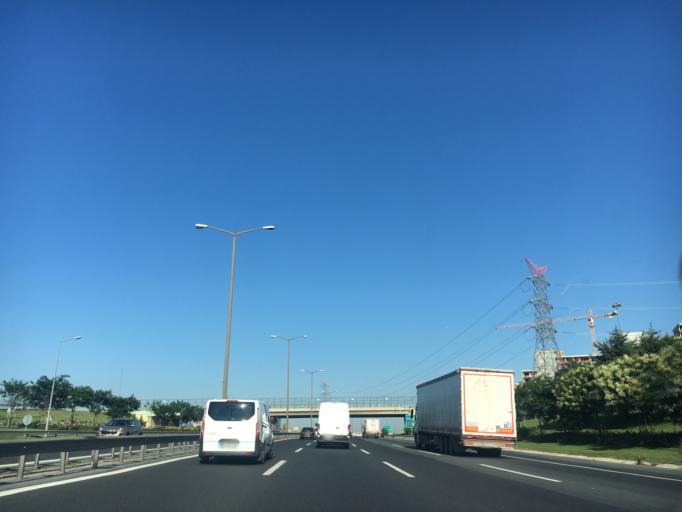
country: TR
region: Istanbul
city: Esenyurt
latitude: 41.0539
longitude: 28.6729
